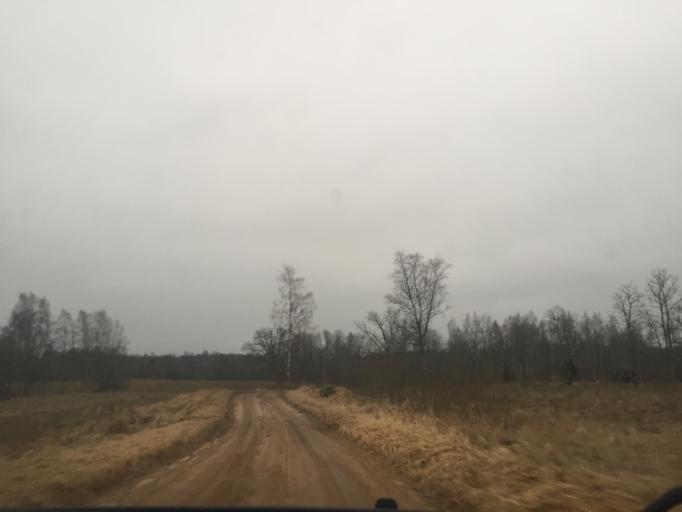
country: LV
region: Ligatne
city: Ligatne
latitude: 57.1293
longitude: 25.1259
